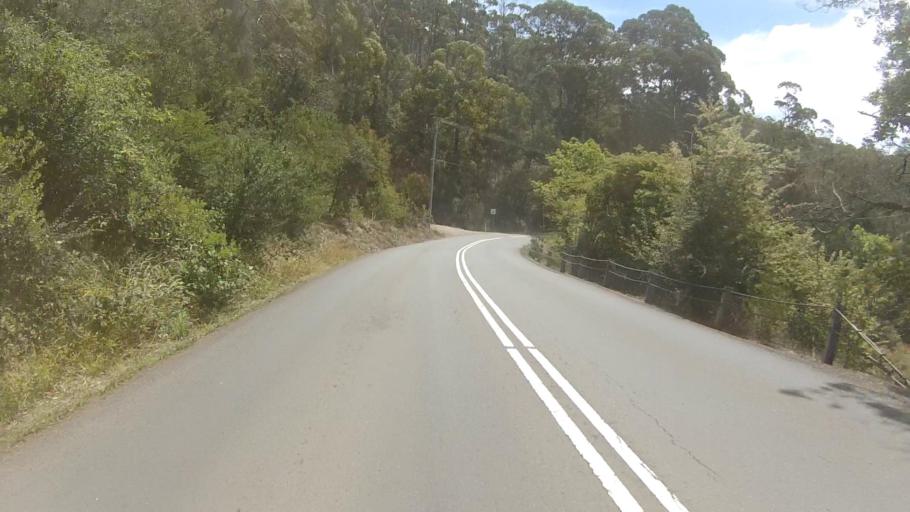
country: AU
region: Tasmania
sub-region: Kingborough
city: Kingston Beach
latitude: -42.9621
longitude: 147.3310
